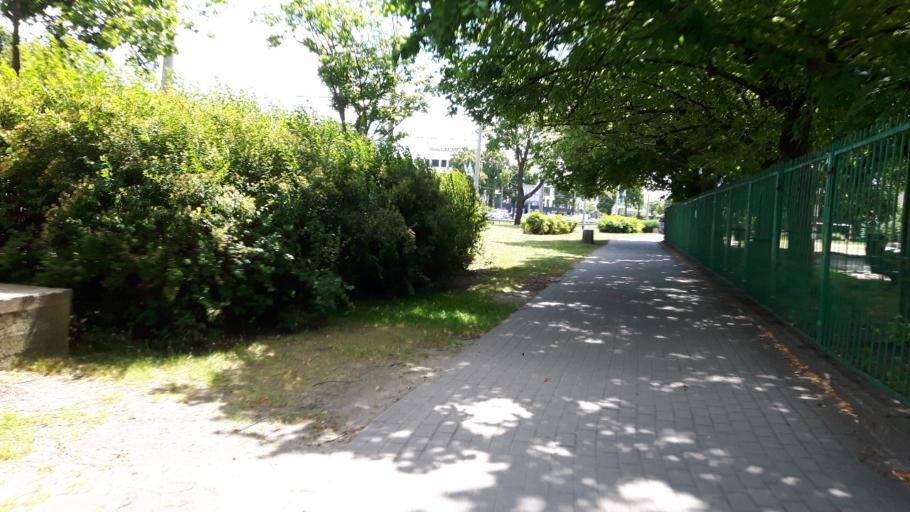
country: PL
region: Pomeranian Voivodeship
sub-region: Gdynia
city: Gdynia
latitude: 54.4823
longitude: 18.5499
